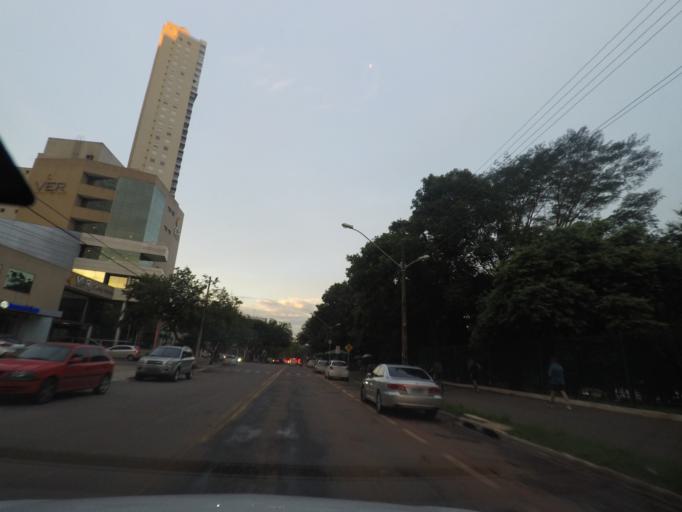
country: BR
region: Goias
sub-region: Goiania
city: Goiania
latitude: -16.7040
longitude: -49.2546
